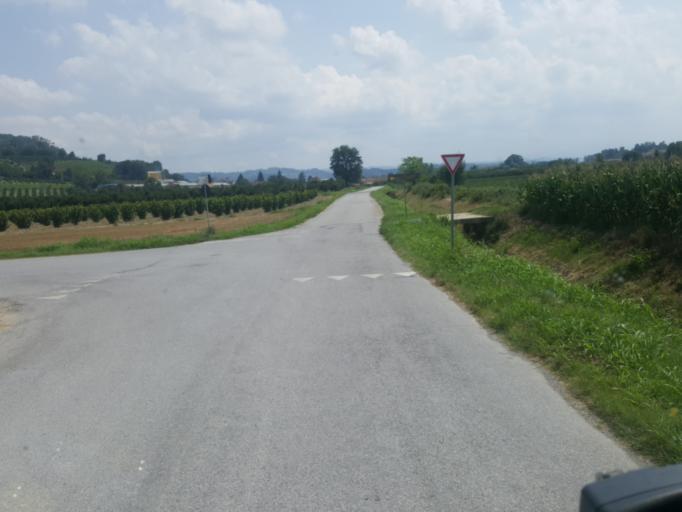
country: IT
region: Piedmont
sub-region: Provincia di Cuneo
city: Novello
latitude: 44.5922
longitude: 7.8987
